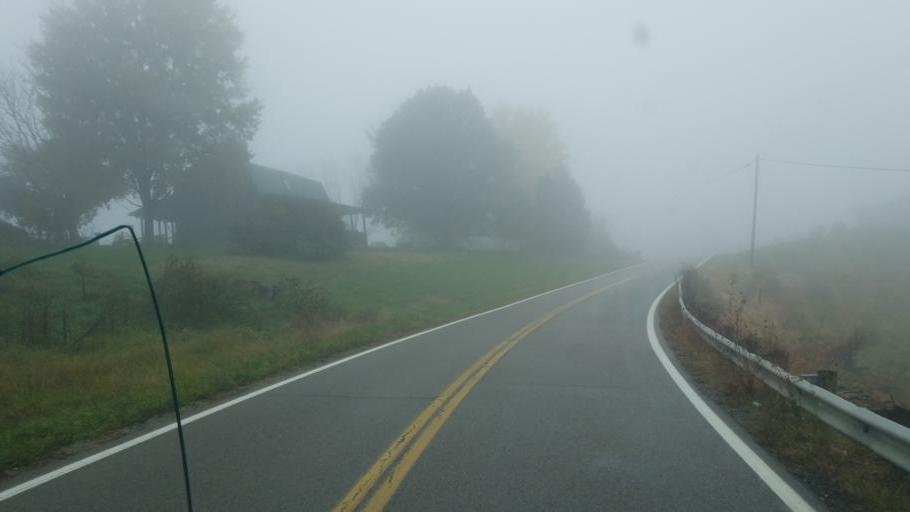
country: US
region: Ohio
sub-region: Morgan County
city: McConnelsville
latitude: 39.5833
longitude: -81.8609
